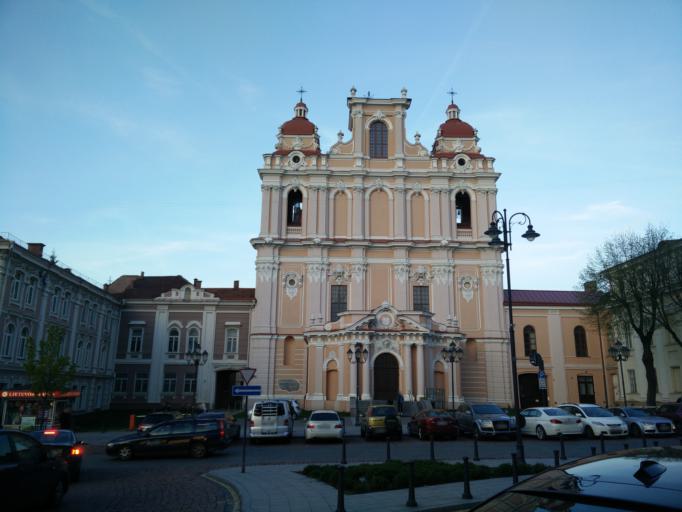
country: LT
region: Vilnius County
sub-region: Vilnius
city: Vilnius
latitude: 54.6776
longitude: 25.2873
